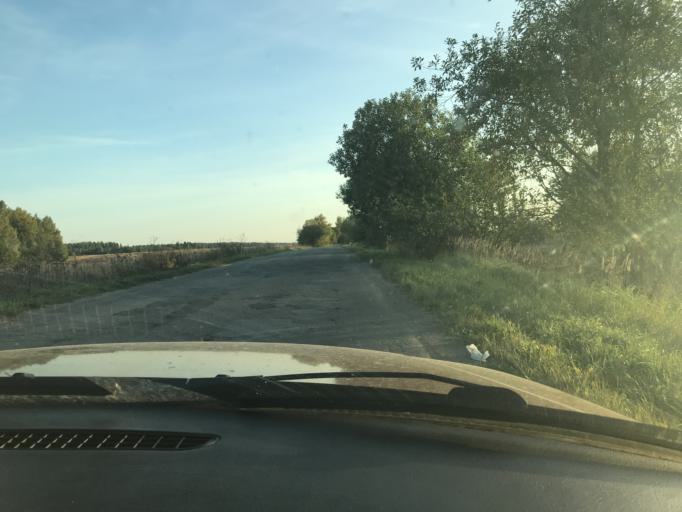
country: RU
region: Kaluga
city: Myatlevo
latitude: 54.7884
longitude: 35.7345
